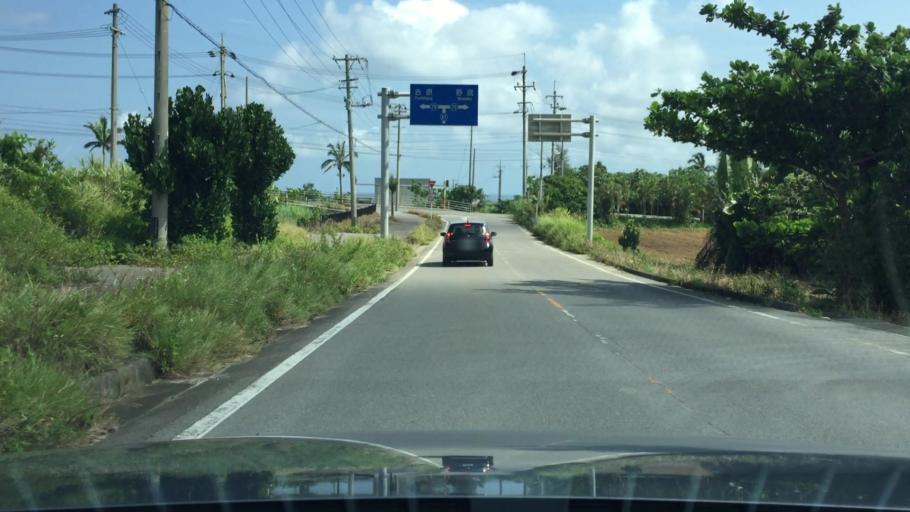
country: JP
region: Okinawa
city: Ishigaki
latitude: 24.4530
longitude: 124.2059
